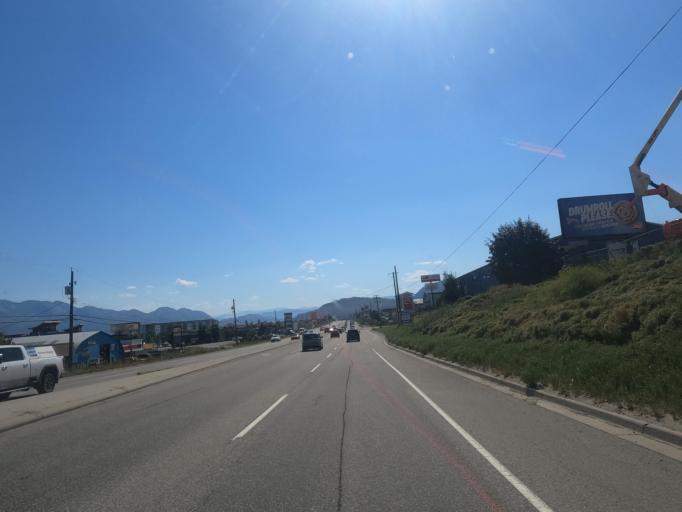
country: CA
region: British Columbia
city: West Kelowna
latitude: 49.8415
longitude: -119.6088
